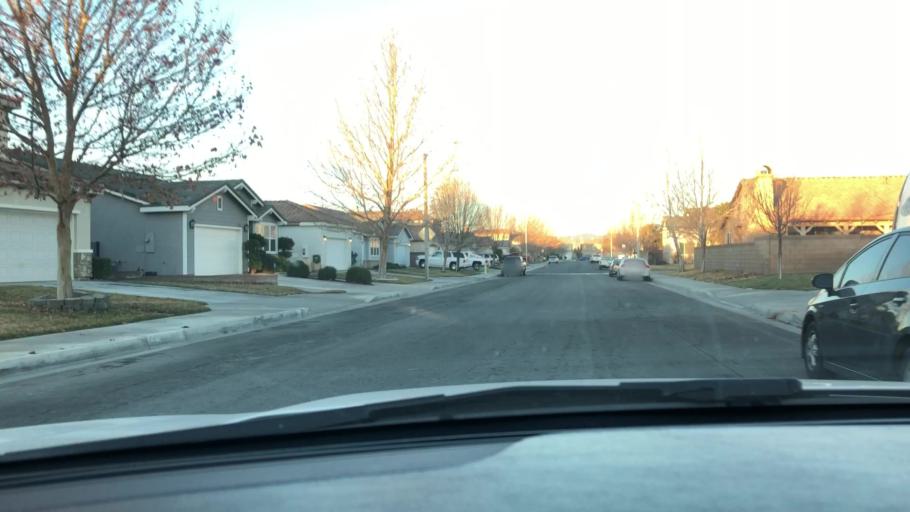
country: US
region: California
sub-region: Los Angeles County
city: Quartz Hill
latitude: 34.6807
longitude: -118.2033
